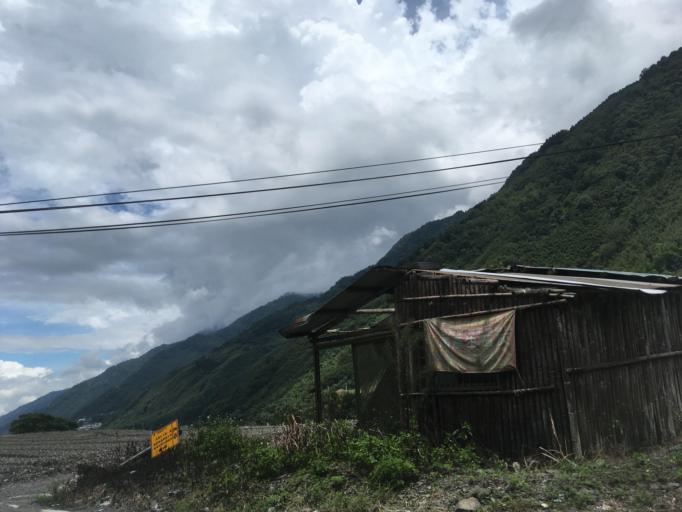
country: TW
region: Taiwan
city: Daxi
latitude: 24.4692
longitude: 121.4101
